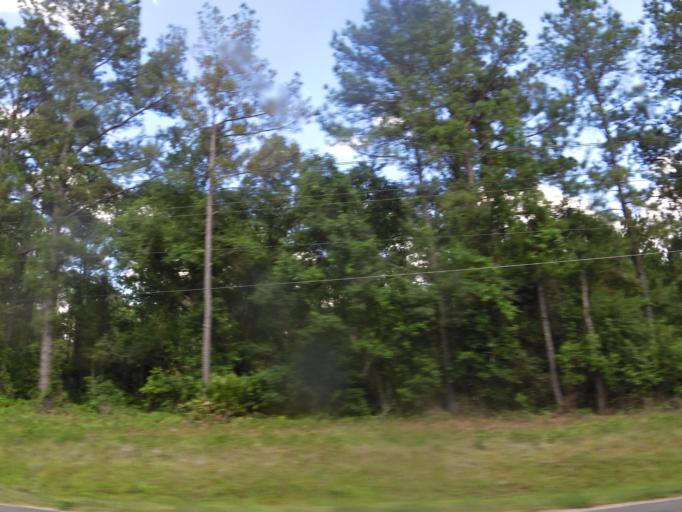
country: US
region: Florida
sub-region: Clay County
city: Keystone Heights
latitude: 29.8454
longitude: -81.9198
